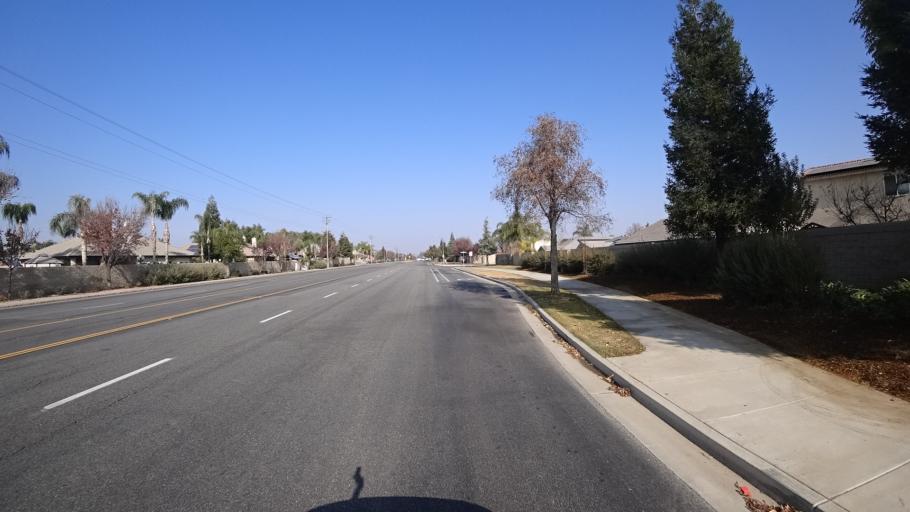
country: US
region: California
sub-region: Kern County
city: Rosedale
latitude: 35.4160
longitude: -119.1277
